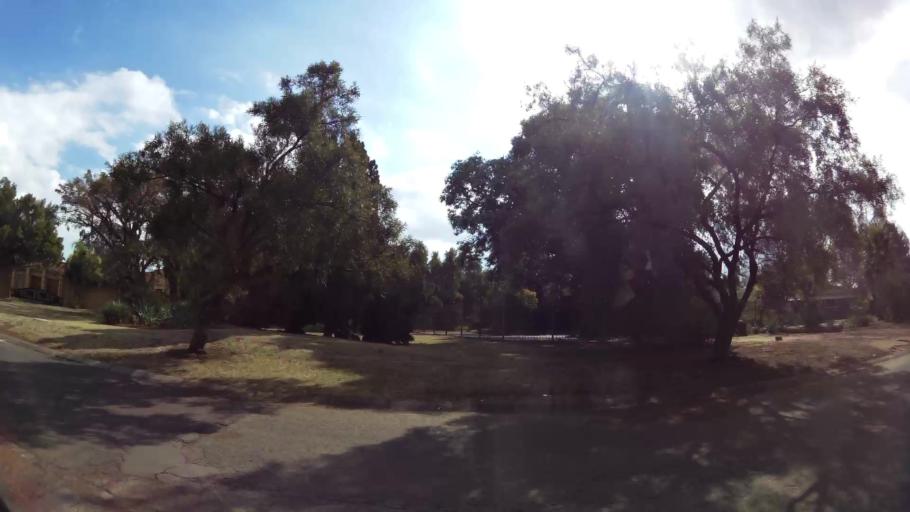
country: ZA
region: Gauteng
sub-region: Sedibeng District Municipality
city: Vanderbijlpark
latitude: -26.7403
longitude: 27.8255
